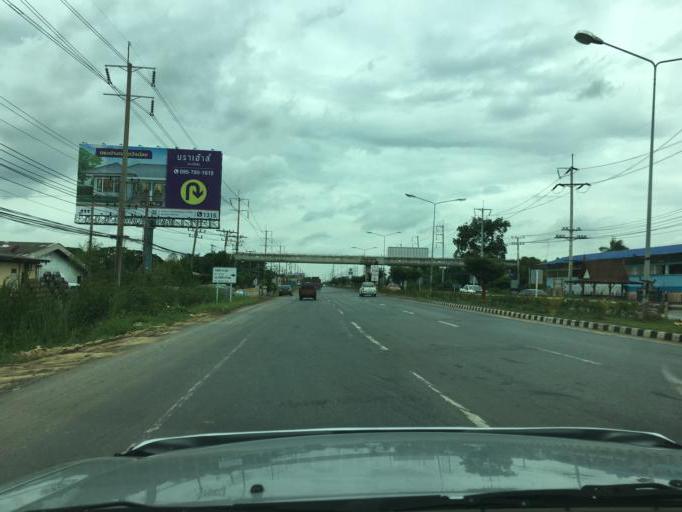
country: TH
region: Phra Nakhon Si Ayutthaya
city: Wang Noi
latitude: 14.2397
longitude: 100.7104
